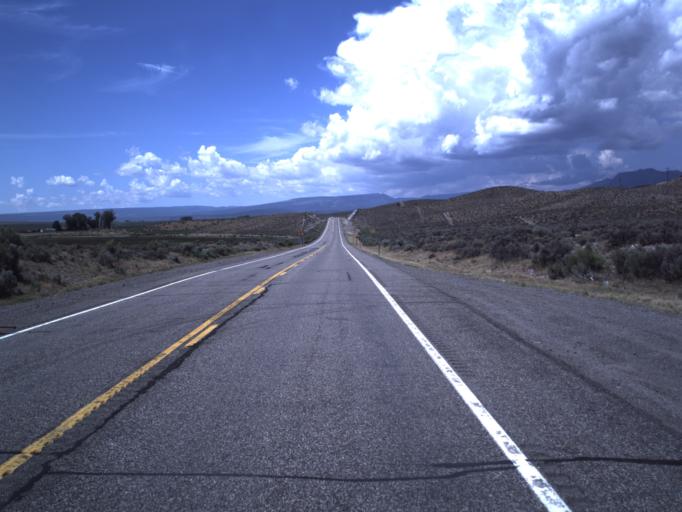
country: US
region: Utah
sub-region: Garfield County
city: Panguitch
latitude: 38.0160
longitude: -112.3698
